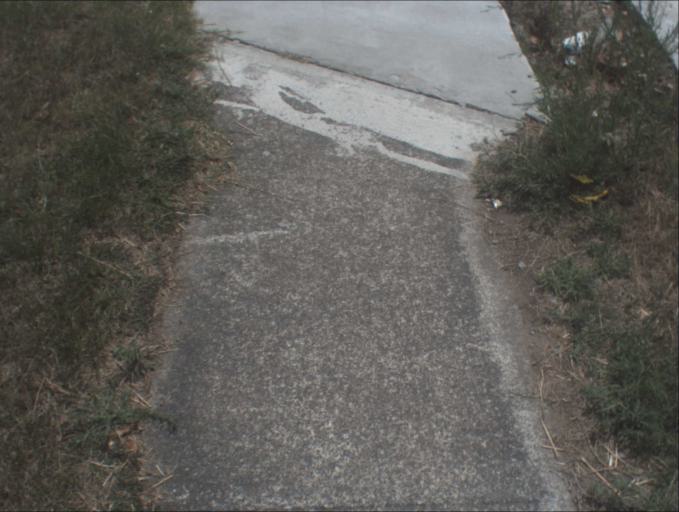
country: AU
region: Queensland
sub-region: Logan
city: Beenleigh
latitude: -27.7170
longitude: 153.1894
